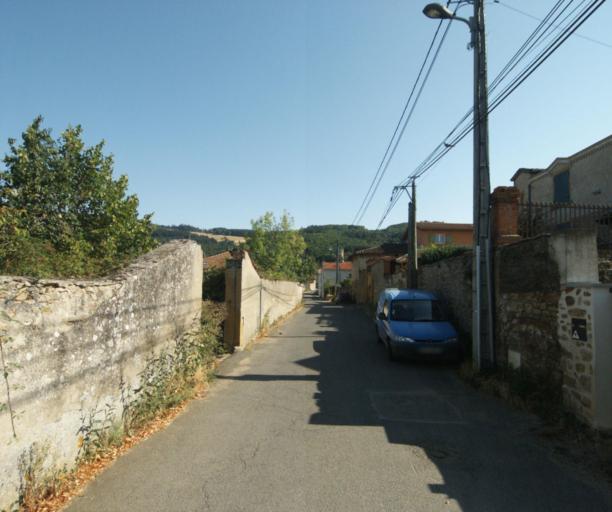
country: FR
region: Rhone-Alpes
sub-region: Departement du Rhone
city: Saint-Pierre-la-Palud
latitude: 45.7730
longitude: 4.6077
